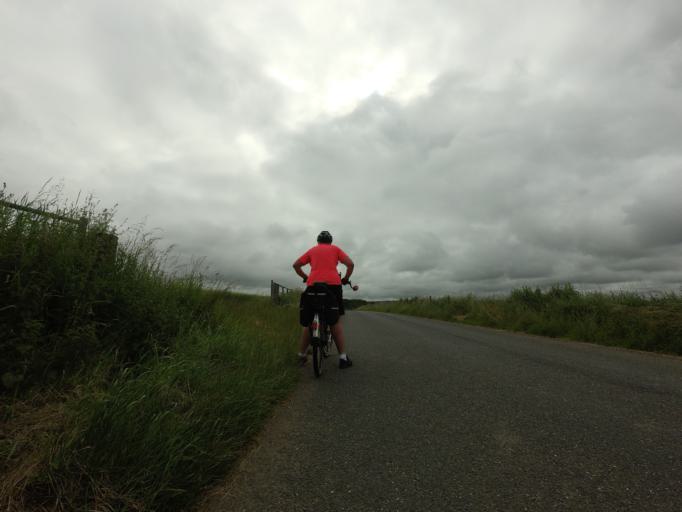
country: GB
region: Scotland
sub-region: Aberdeenshire
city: Turriff
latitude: 57.5343
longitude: -2.4248
